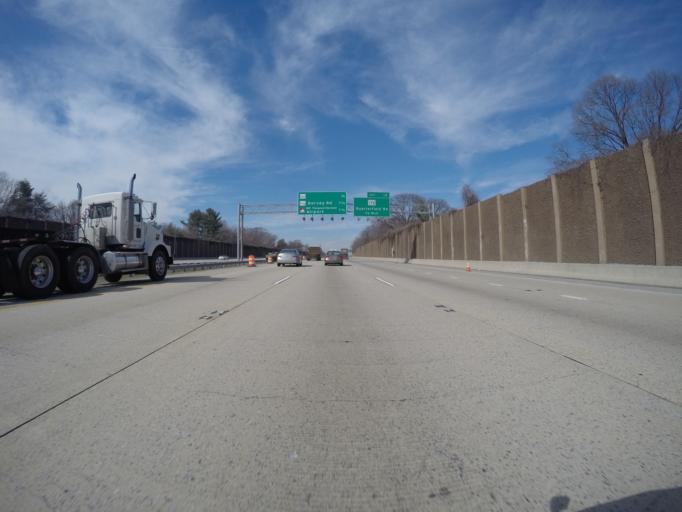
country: US
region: Maryland
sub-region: Anne Arundel County
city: South Gate
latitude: 39.1319
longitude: -76.6427
